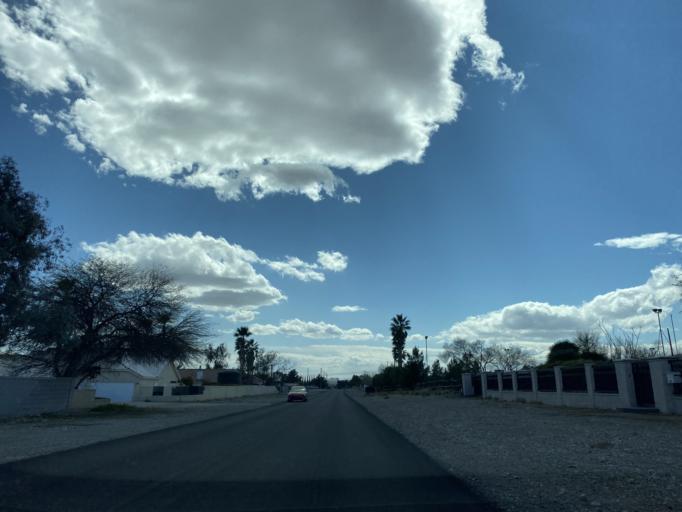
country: US
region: Nevada
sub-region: Clark County
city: Summerlin South
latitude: 36.2682
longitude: -115.2883
